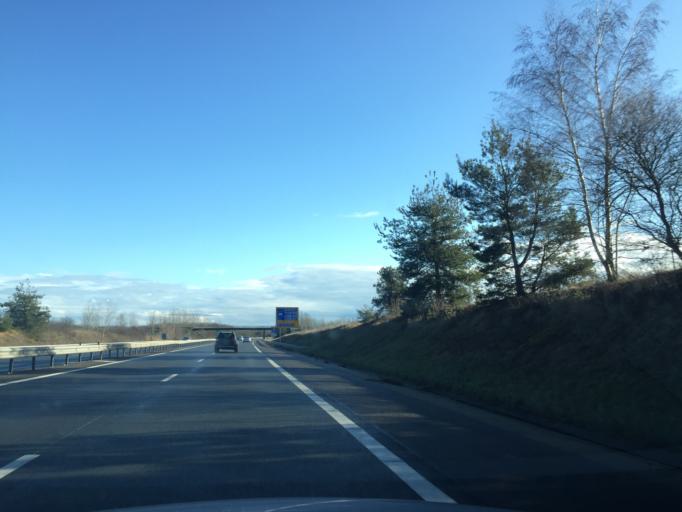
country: FR
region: Rhone-Alpes
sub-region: Departement de la Loire
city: Saint-Germain-Laval
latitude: 45.8495
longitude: 4.0744
